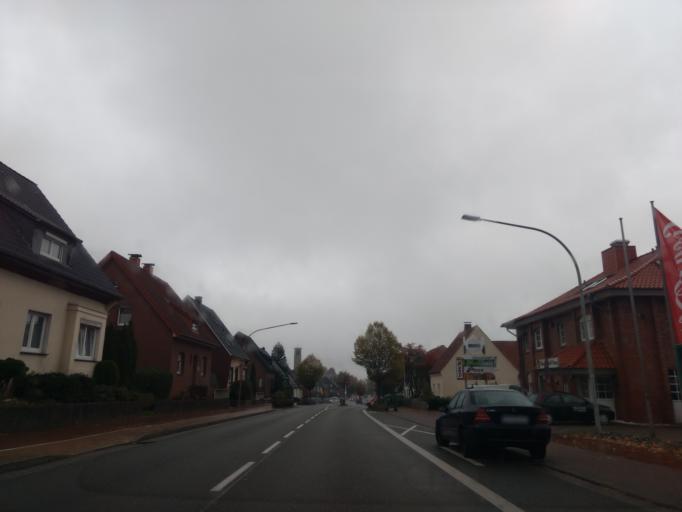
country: DE
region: Lower Saxony
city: Georgsmarienhutte
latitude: 52.1878
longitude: 8.0668
